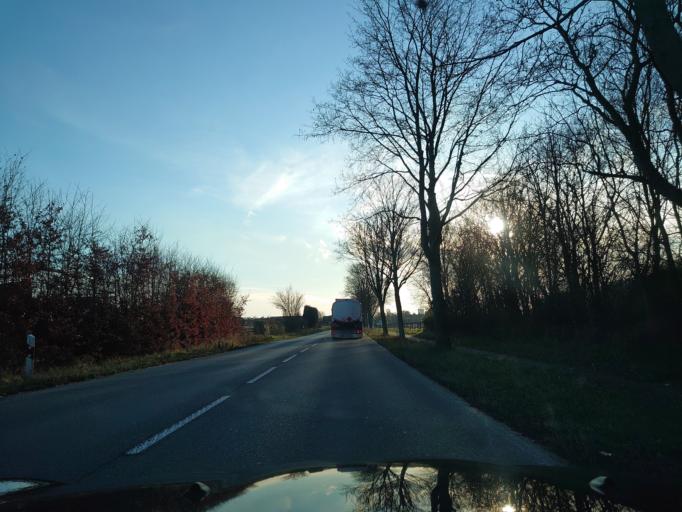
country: DE
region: North Rhine-Westphalia
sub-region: Regierungsbezirk Dusseldorf
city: Rommerskirchen
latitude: 51.0603
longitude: 6.7195
